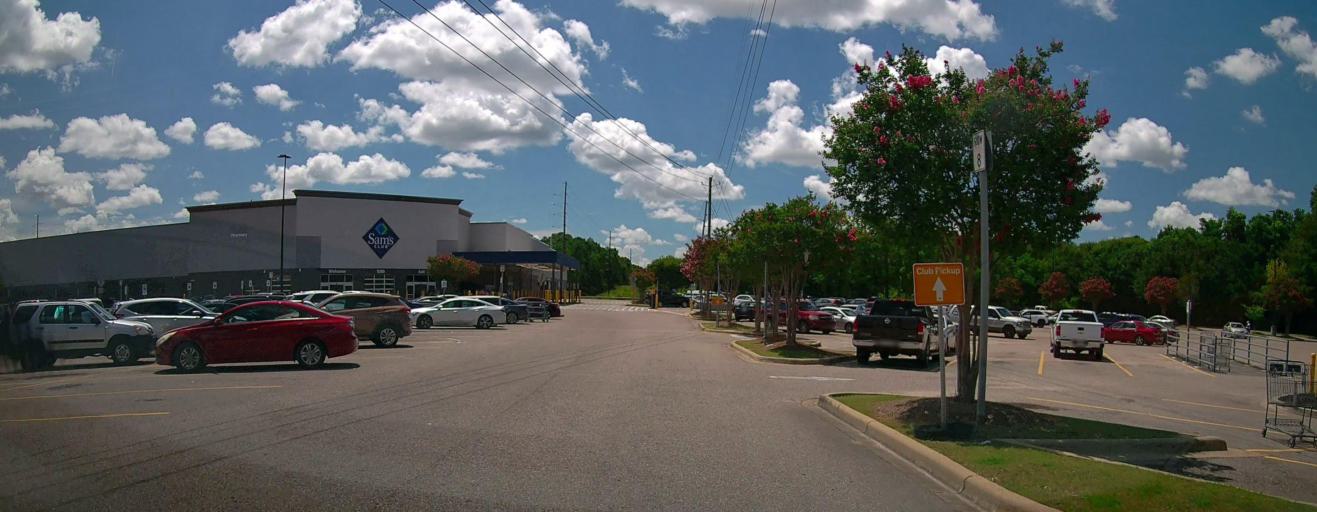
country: US
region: Alabama
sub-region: Montgomery County
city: Montgomery
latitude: 32.3658
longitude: -86.2143
